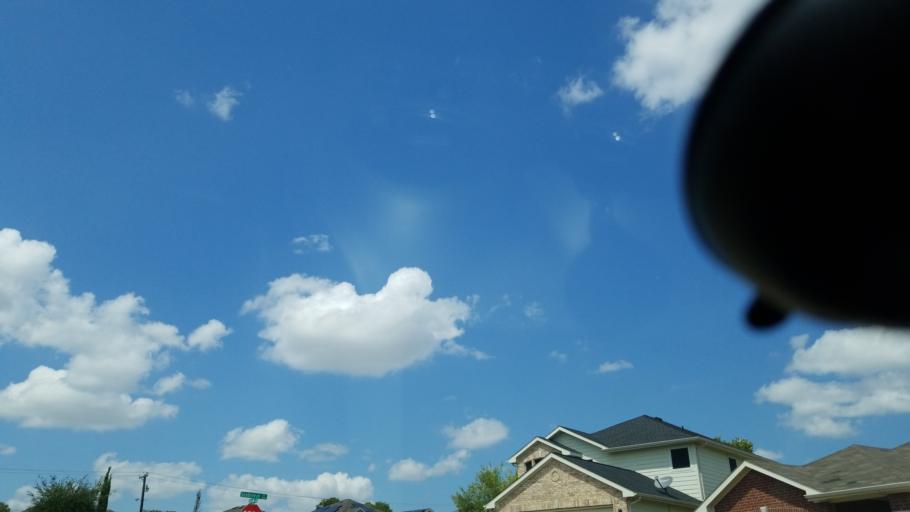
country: US
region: Texas
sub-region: Dallas County
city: Grand Prairie
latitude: 32.7227
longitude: -96.9762
